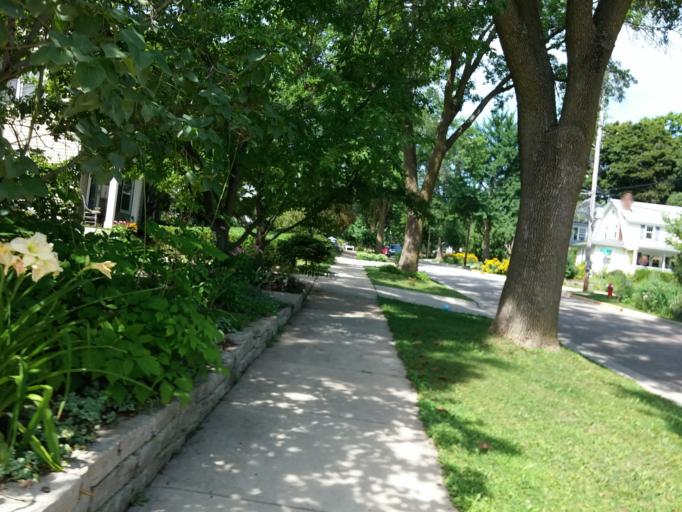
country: US
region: Wisconsin
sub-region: Dane County
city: Shorewood Hills
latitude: 43.0654
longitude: -89.4260
